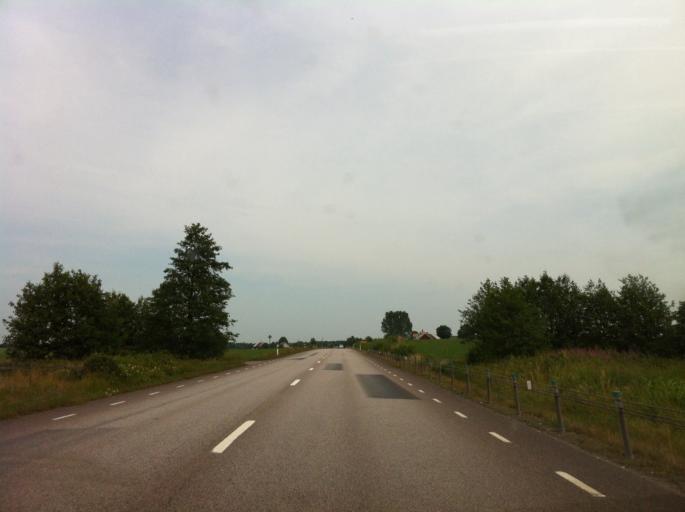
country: SE
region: Kalmar
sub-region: Torsas Kommun
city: Torsas
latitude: 56.3267
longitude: 16.0385
